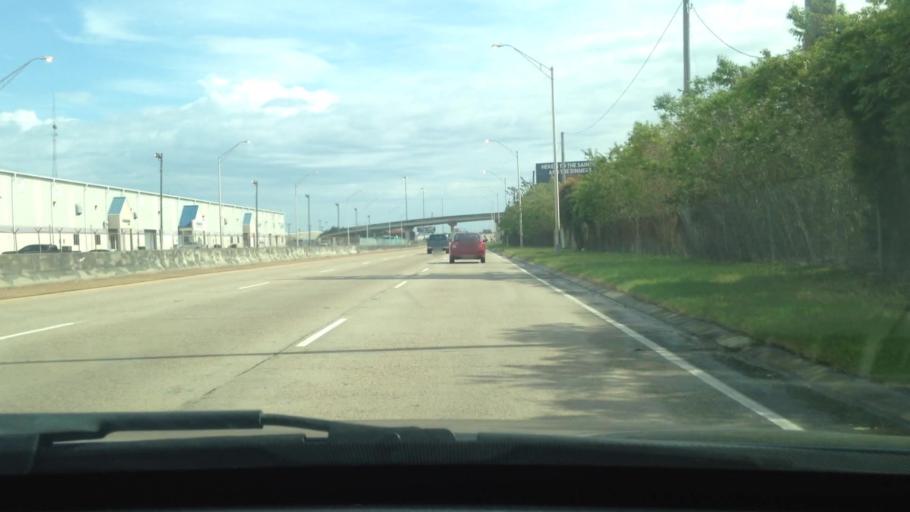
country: US
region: Louisiana
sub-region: Jefferson Parish
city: Jefferson
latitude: 29.9700
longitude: -90.1495
